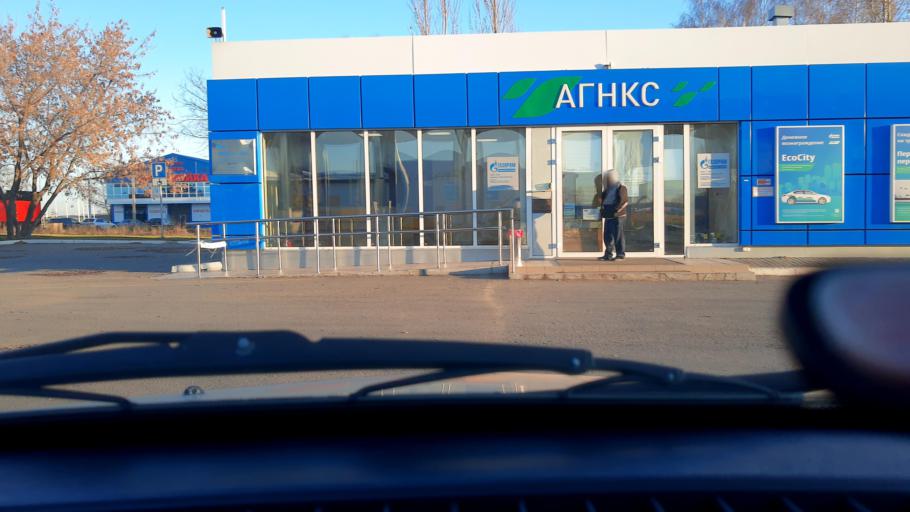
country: RU
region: Bashkortostan
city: Mikhaylovka
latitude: 54.8001
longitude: 55.8593
